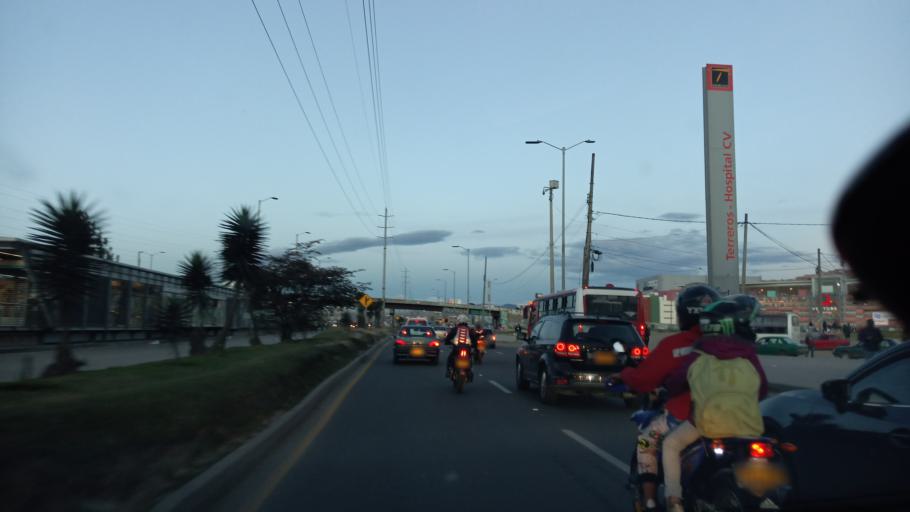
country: CO
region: Cundinamarca
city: Soacha
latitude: 4.5888
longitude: -74.1995
